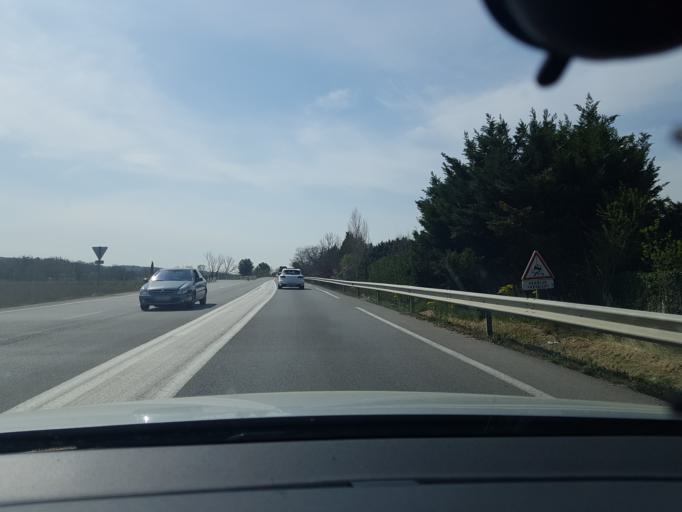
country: FR
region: Provence-Alpes-Cote d'Azur
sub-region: Departement des Bouches-du-Rhone
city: Chateauneuf-le-Rouge
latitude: 43.4784
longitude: 5.5420
